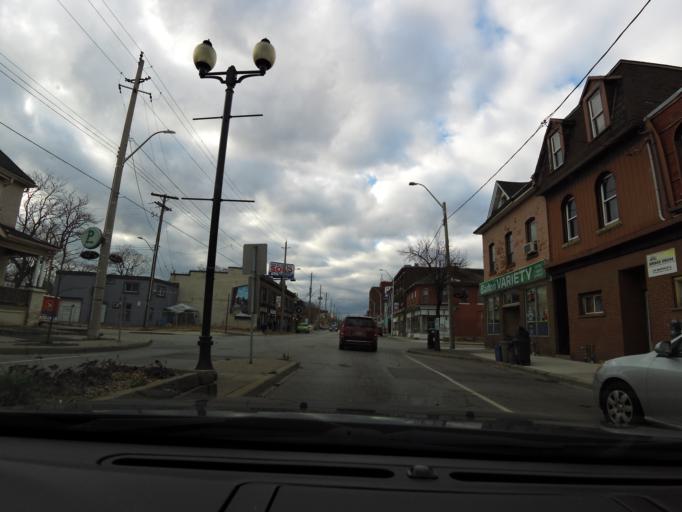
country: CA
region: Ontario
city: Hamilton
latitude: 43.2606
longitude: -79.8517
